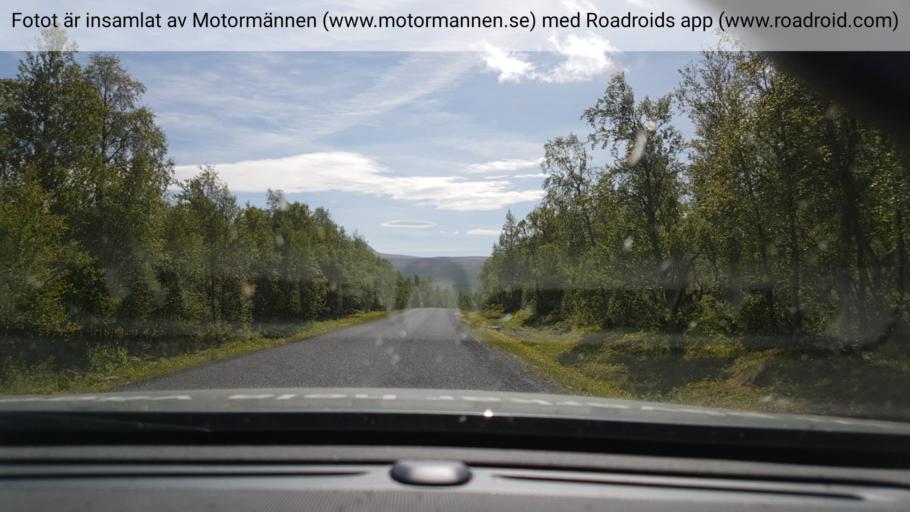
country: NO
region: Nordland
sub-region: Hattfjelldal
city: Hattfjelldal
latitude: 65.3455
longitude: 15.0970
